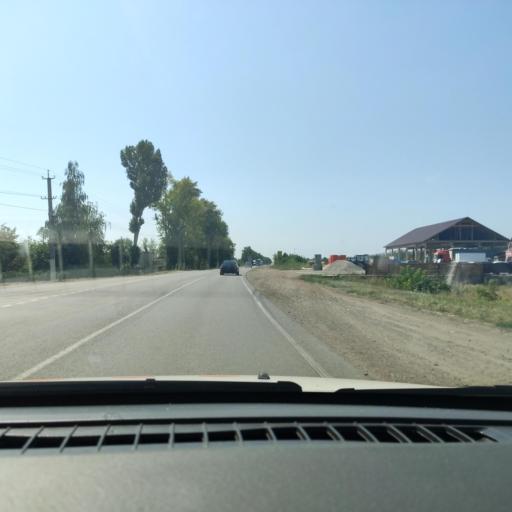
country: RU
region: Voronezj
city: Imeni Pervogo Maya
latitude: 50.7141
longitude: 39.4085
